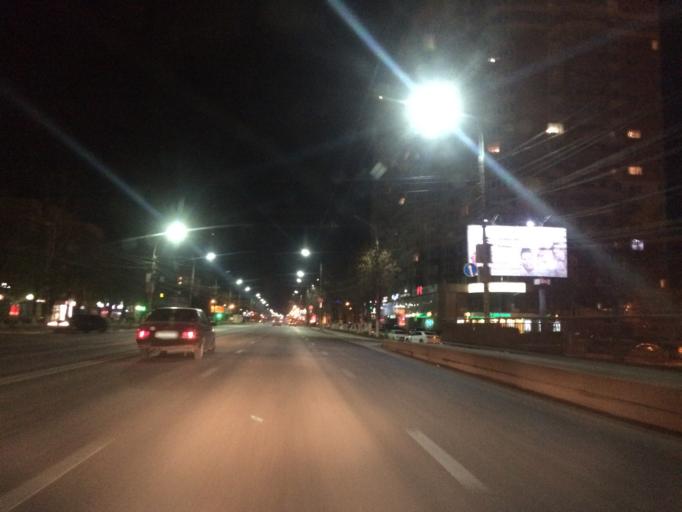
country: RU
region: Tula
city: Mendeleyevskiy
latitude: 54.1566
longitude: 37.5850
